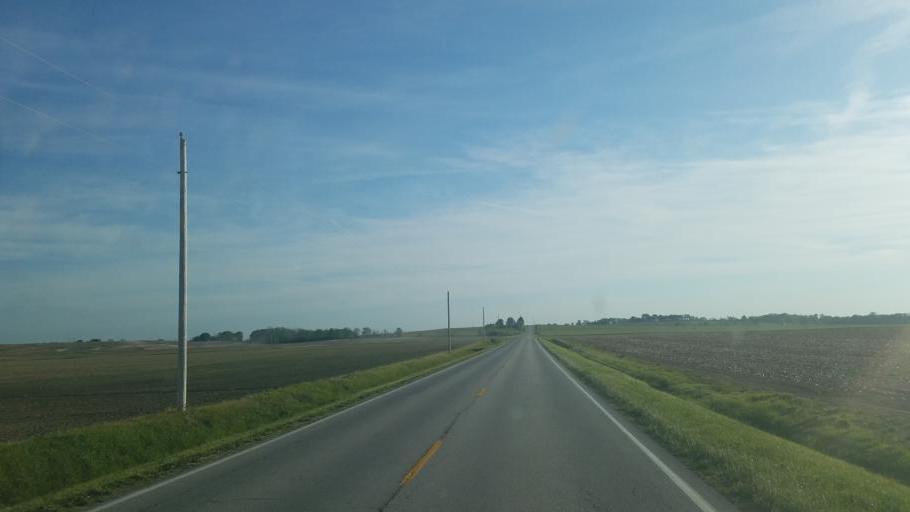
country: US
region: Ohio
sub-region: Highland County
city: Greenfield
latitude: 39.3786
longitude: -83.3453
